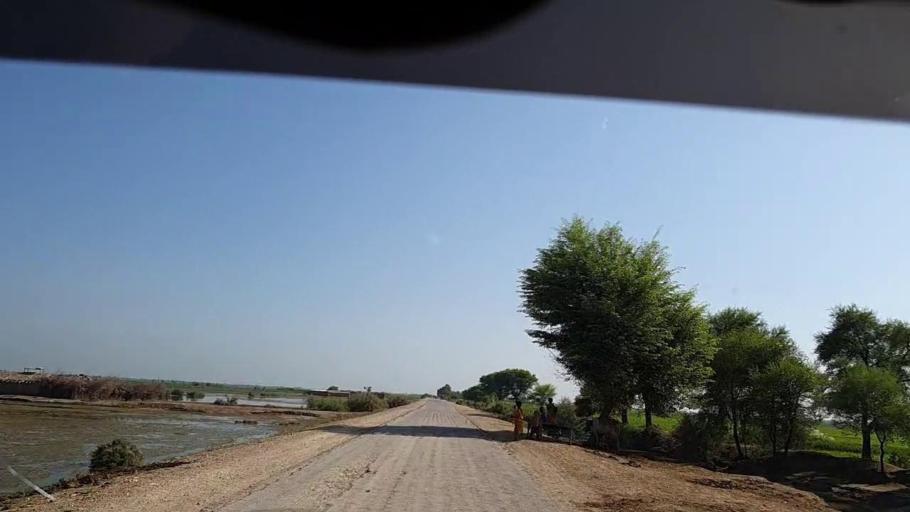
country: PK
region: Sindh
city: Tangwani
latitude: 28.3607
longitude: 69.0130
